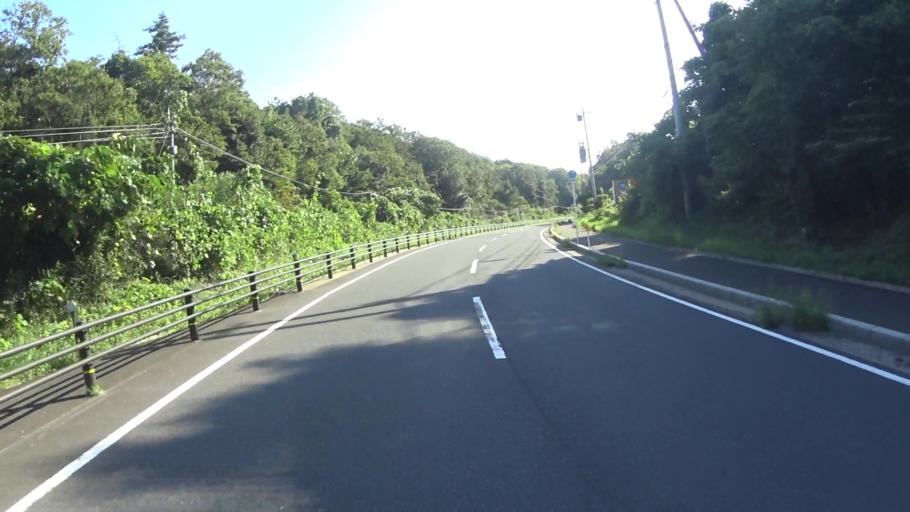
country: JP
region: Hyogo
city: Toyooka
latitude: 35.6475
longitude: 134.9512
